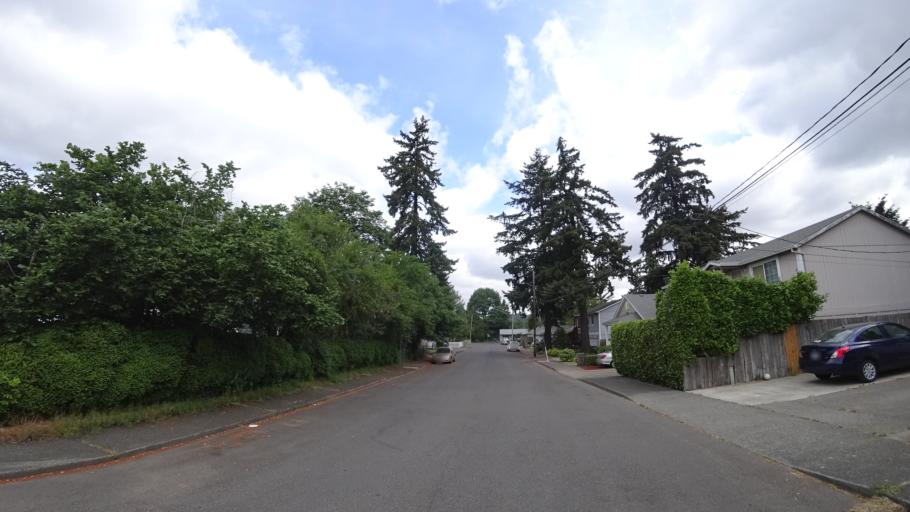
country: US
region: Oregon
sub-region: Multnomah County
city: Lents
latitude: 45.4780
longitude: -122.5609
